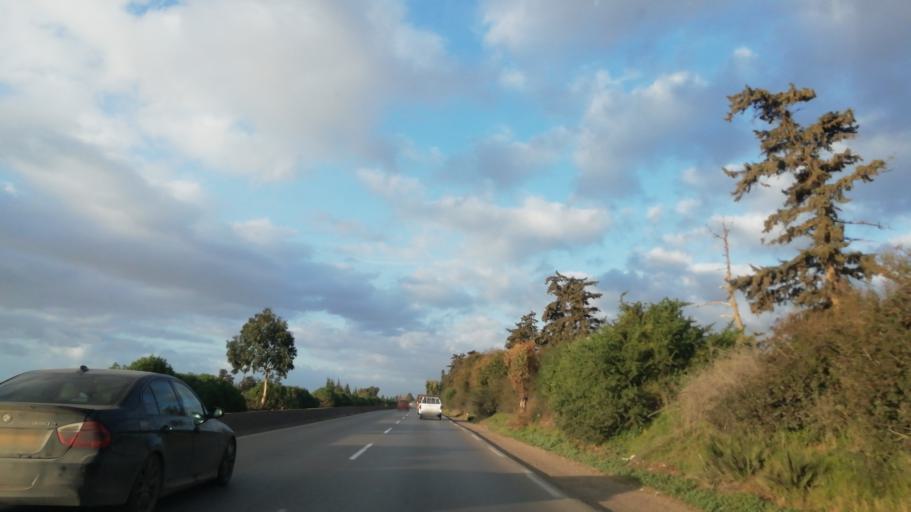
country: DZ
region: Oran
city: Bou Tlelis
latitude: 35.5989
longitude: -0.7758
